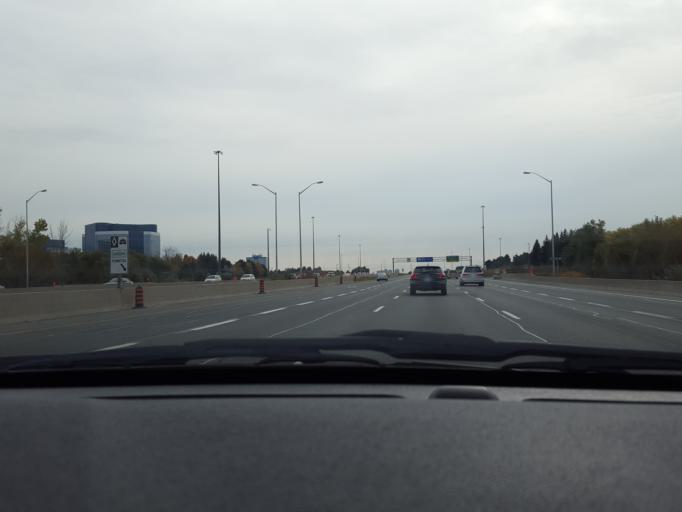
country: CA
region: Ontario
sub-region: York
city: Richmond Hill
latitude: 43.8553
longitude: -79.3732
